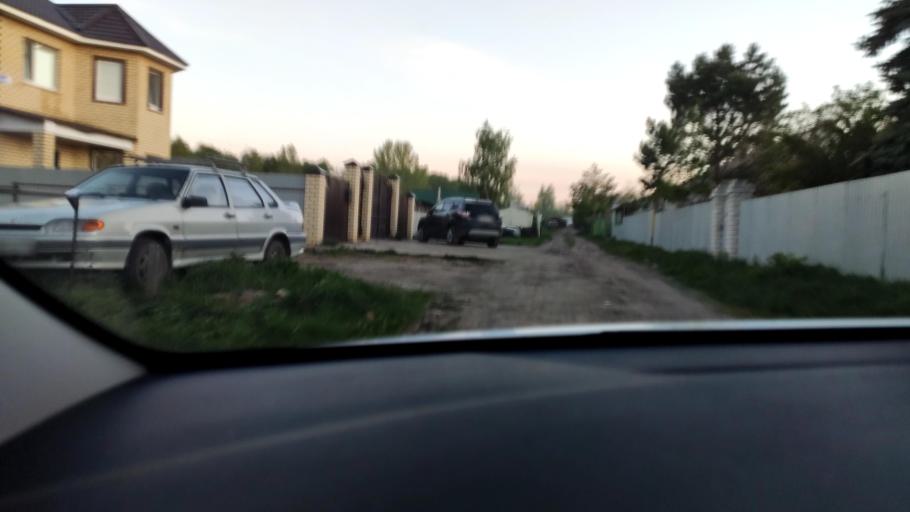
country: RU
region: Tatarstan
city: Stolbishchi
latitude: 55.7389
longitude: 49.2728
